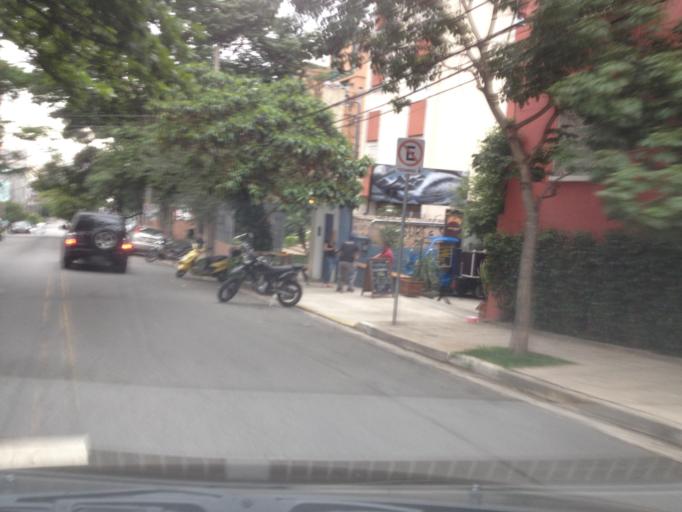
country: BR
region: Sao Paulo
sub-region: Sao Paulo
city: Sao Paulo
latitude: -23.5541
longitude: -46.6915
